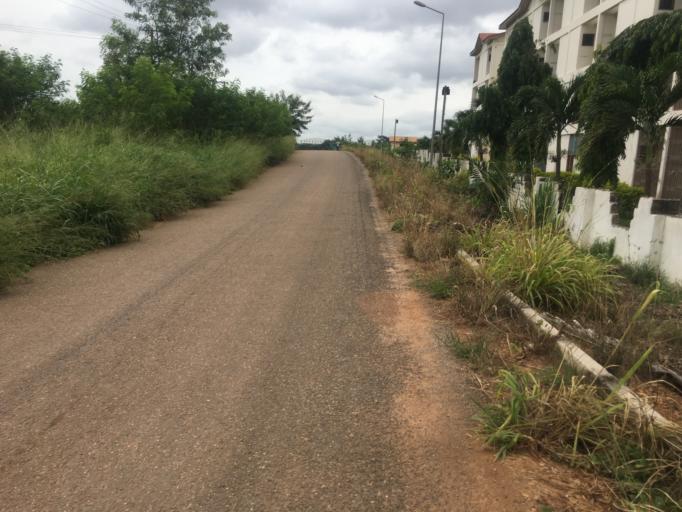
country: GH
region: Ashanti
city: Mamponteng
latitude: 6.6890
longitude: -1.5551
